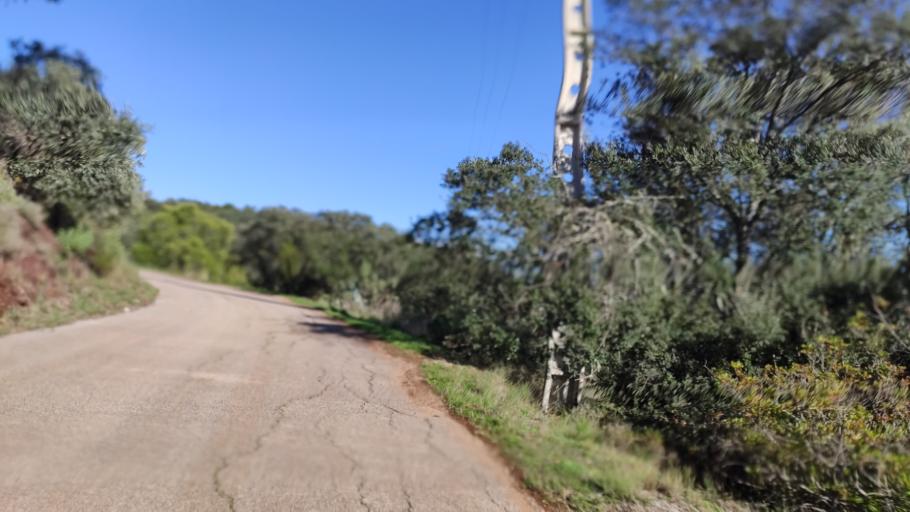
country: PT
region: Faro
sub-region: Sao Bras de Alportel
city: Sao Bras de Alportel
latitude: 37.1585
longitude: -7.9032
